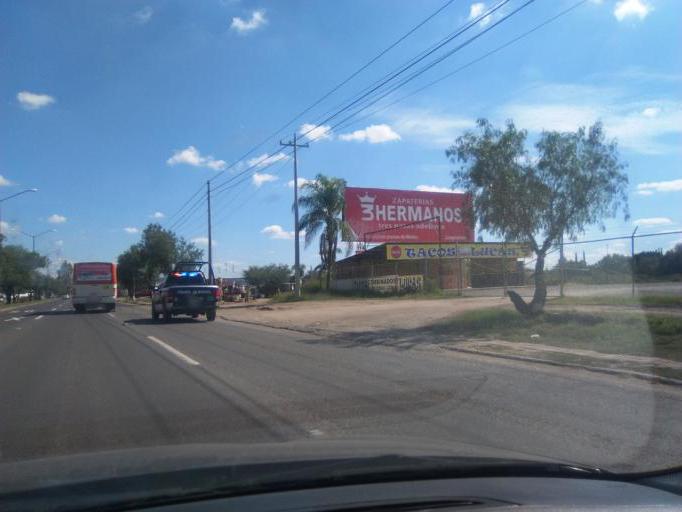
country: MX
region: Guanajuato
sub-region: Leon
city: Fraccionamiento Paraiso Real
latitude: 21.0779
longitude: -101.6054
